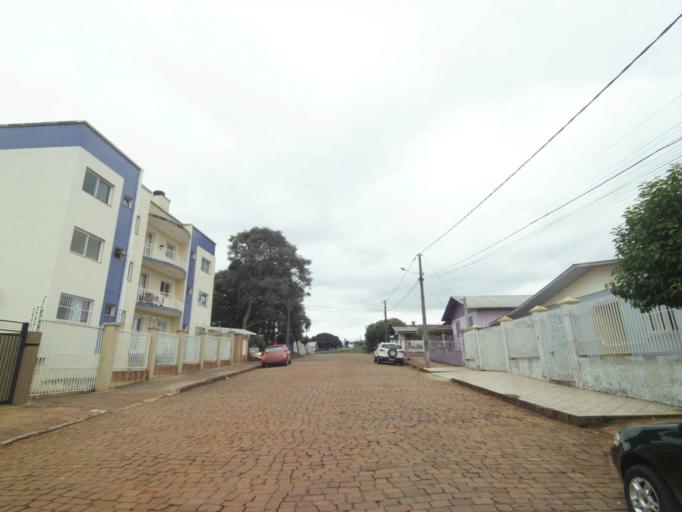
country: BR
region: Rio Grande do Sul
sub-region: Lagoa Vermelha
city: Lagoa Vermelha
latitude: -28.2049
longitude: -51.5253
